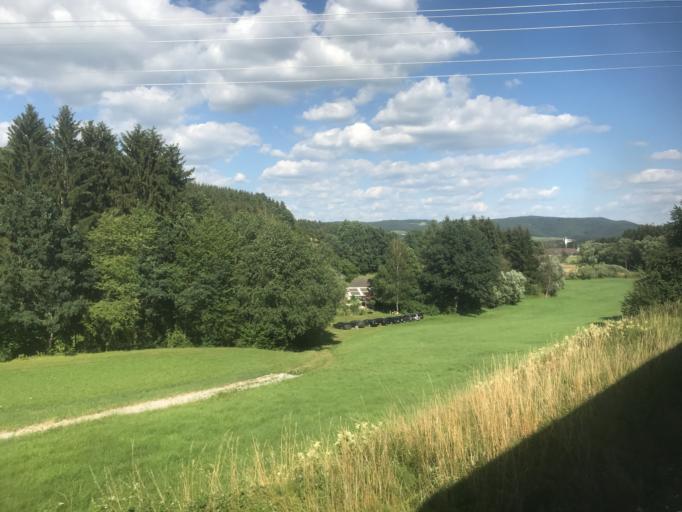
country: AT
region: Upper Austria
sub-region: Politischer Bezirk Freistadt
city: Freistadt
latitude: 48.4985
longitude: 14.4670
